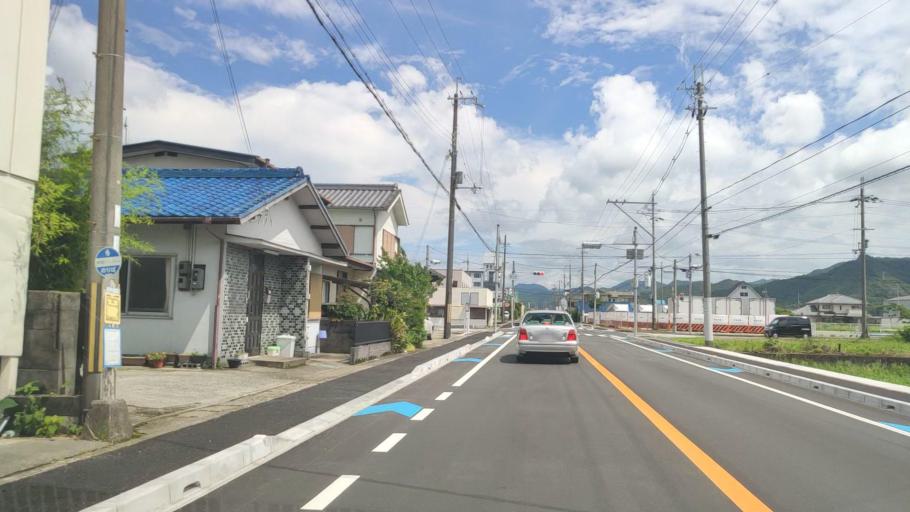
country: JP
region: Hyogo
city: Nishiwaki
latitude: 35.0055
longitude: 134.9622
